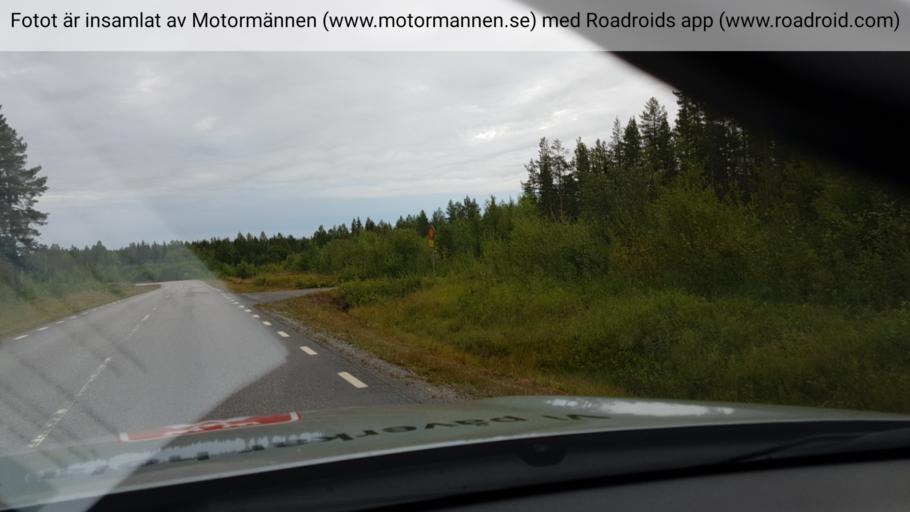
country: SE
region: Norrbotten
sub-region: Bodens Kommun
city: Boden
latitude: 65.7663
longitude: 21.6186
